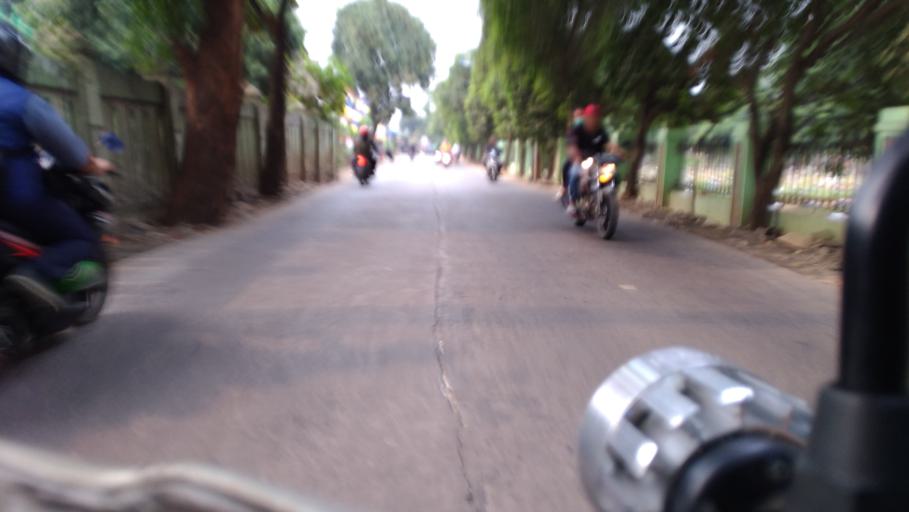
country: ID
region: West Java
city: Cileungsir
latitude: -6.3603
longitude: 106.9085
